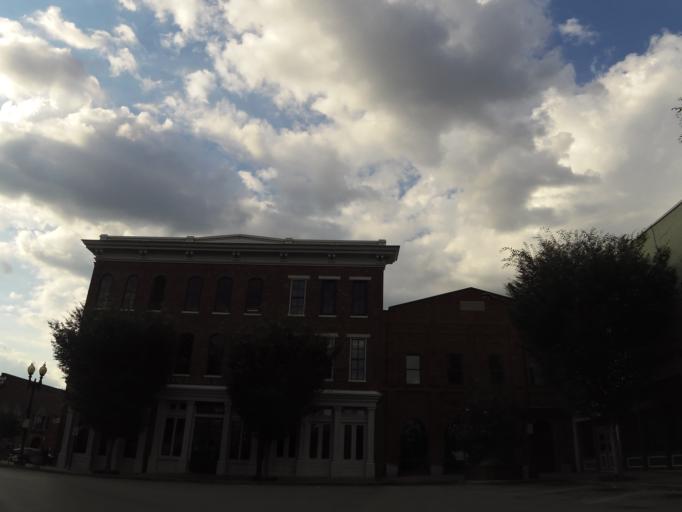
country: US
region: Tennessee
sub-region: Maury County
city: Columbia
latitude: 35.6149
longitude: -87.0334
